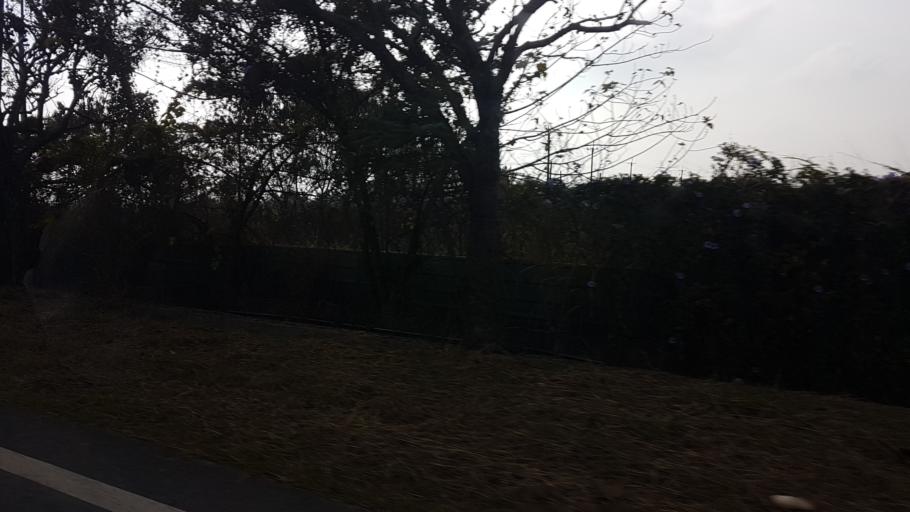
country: TW
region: Taiwan
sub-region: Chiayi
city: Jiayi Shi
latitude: 23.4052
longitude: 120.4295
